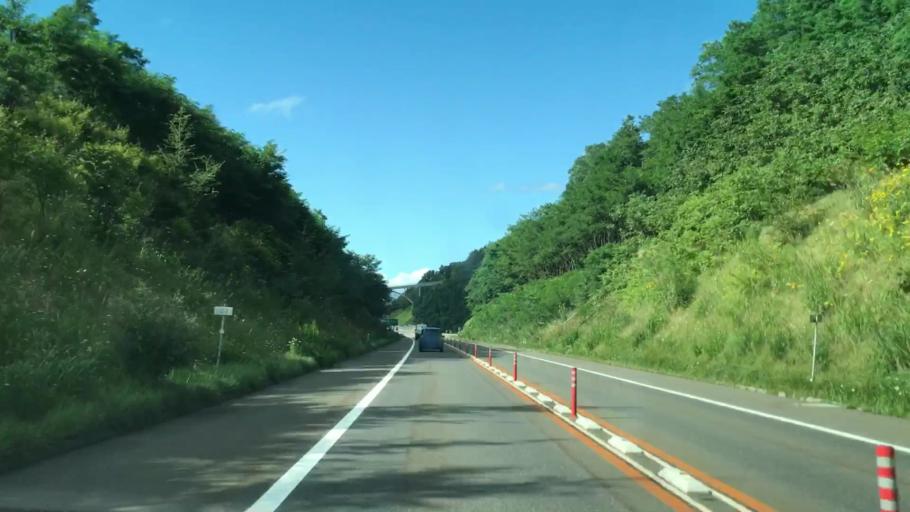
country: JP
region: Hokkaido
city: Date
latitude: 42.4565
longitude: 140.9125
